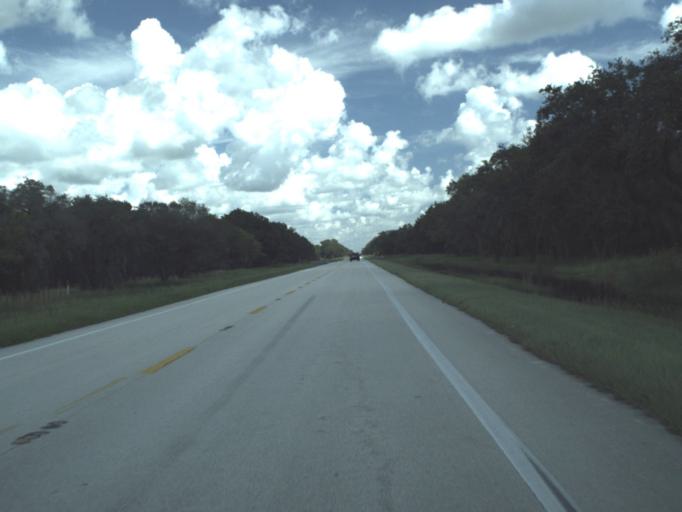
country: US
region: Florida
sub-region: Hendry County
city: Port LaBelle
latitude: 26.8607
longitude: -81.3711
